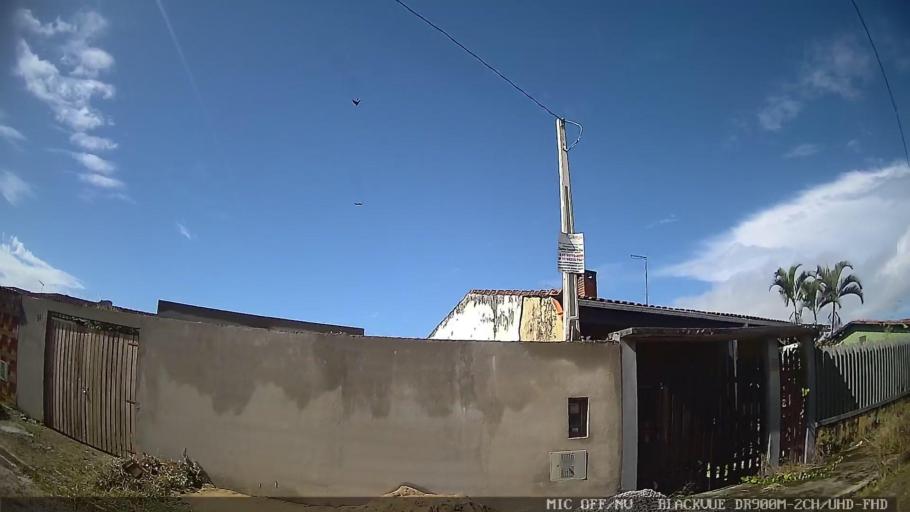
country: BR
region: Sao Paulo
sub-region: Itanhaem
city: Itanhaem
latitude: -24.2408
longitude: -46.8851
